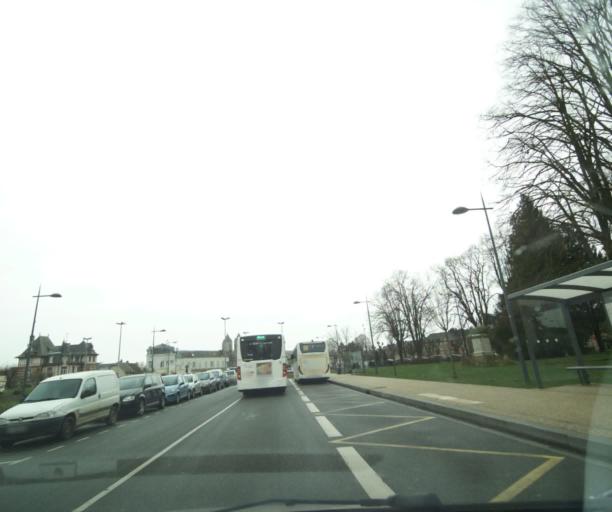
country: FR
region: Picardie
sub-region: Departement de l'Oise
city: Noyon
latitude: 49.5779
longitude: 3.0059
